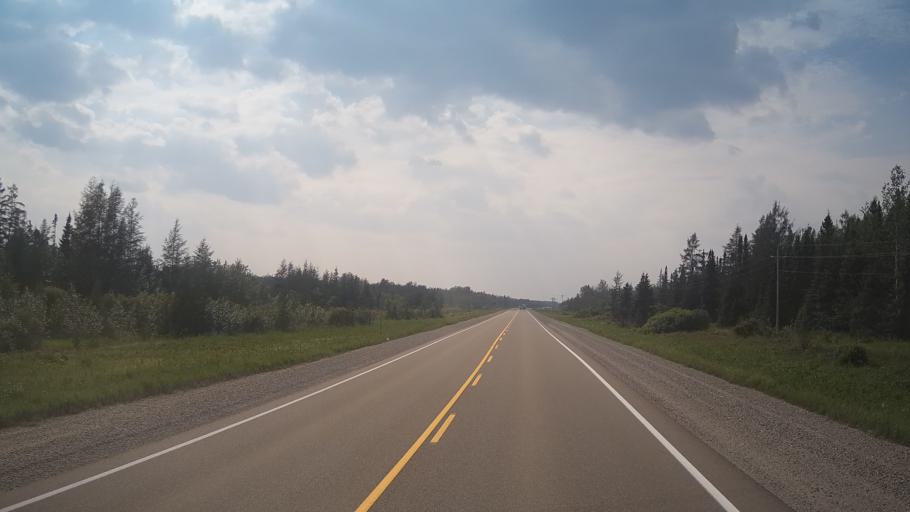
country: CA
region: Ontario
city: Kapuskasing
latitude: 49.5065
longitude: -82.7544
